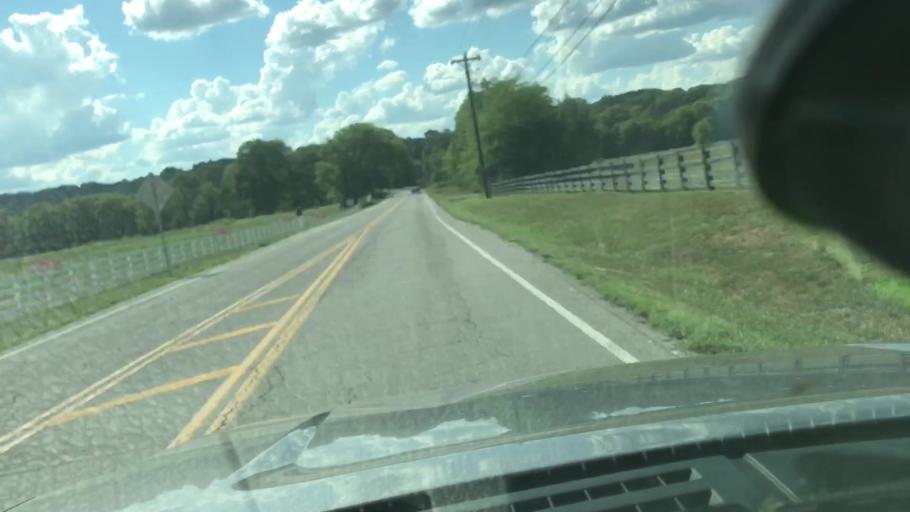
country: US
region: Tennessee
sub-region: Davidson County
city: Forest Hills
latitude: 36.0290
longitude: -86.9181
